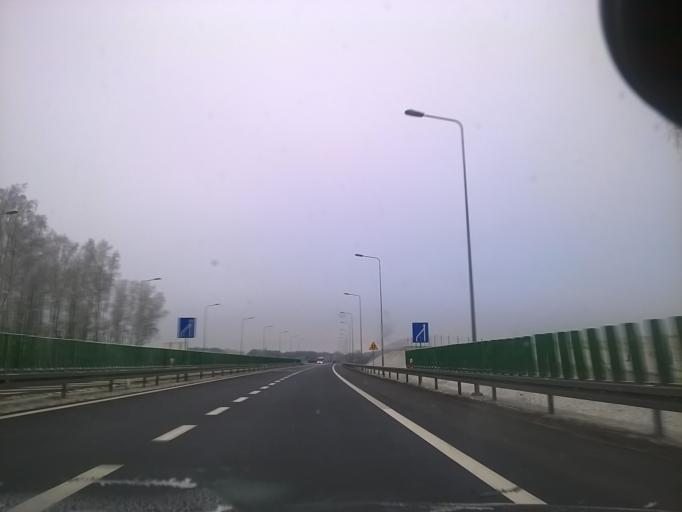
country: PL
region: Warmian-Masurian Voivodeship
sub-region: Powiat olsztynski
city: Barczewo
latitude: 53.8269
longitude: 20.8017
